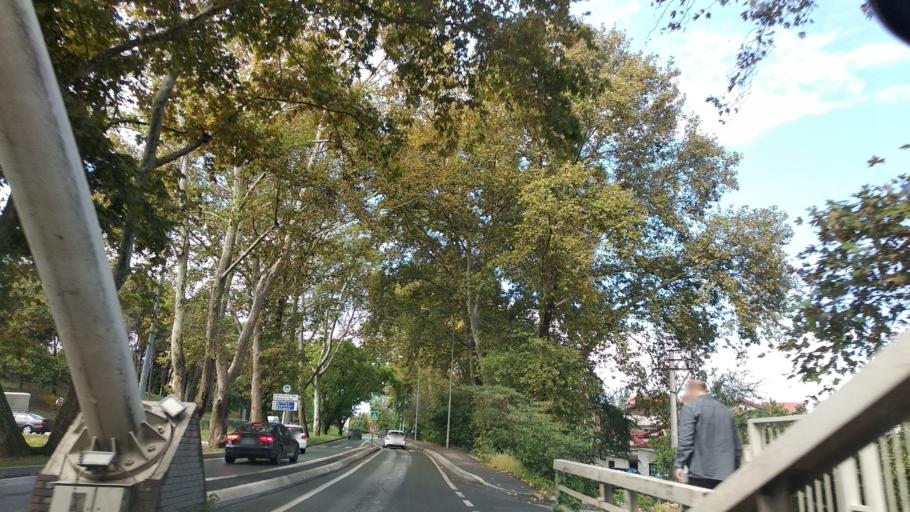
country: TR
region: Sakarya
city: Adapazari
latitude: 40.7558
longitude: 30.3756
